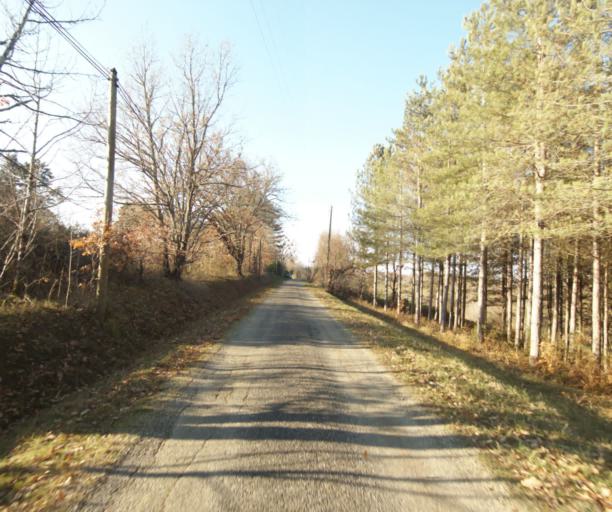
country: FR
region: Midi-Pyrenees
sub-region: Departement du Tarn-et-Garonne
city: Moissac
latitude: 44.1419
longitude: 1.0712
